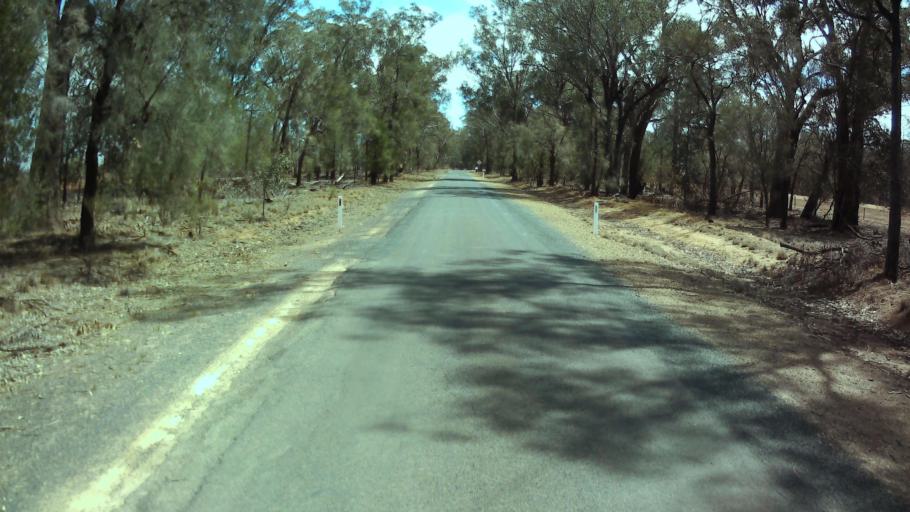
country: AU
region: New South Wales
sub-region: Weddin
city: Grenfell
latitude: -33.6463
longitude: 148.1919
